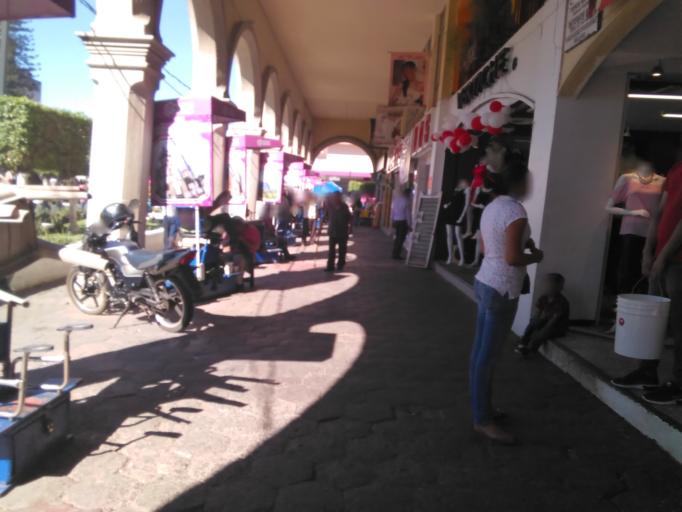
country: MX
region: Nayarit
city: Tepic
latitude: 21.5124
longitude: -104.8919
